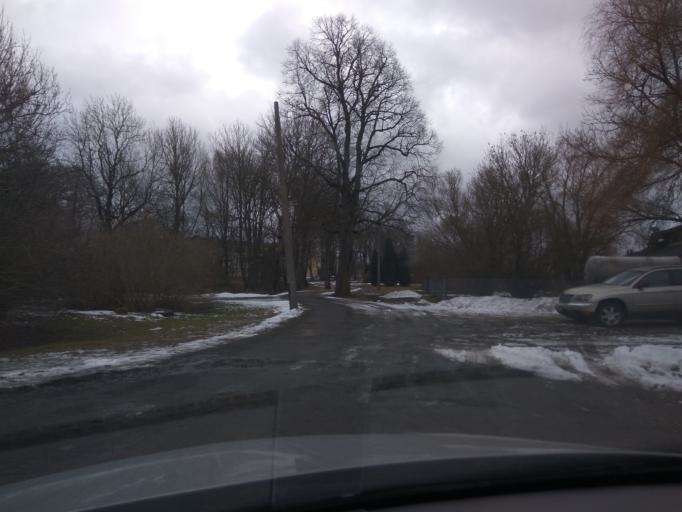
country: LV
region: Ventspils
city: Ventspils
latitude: 57.3325
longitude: 21.6427
